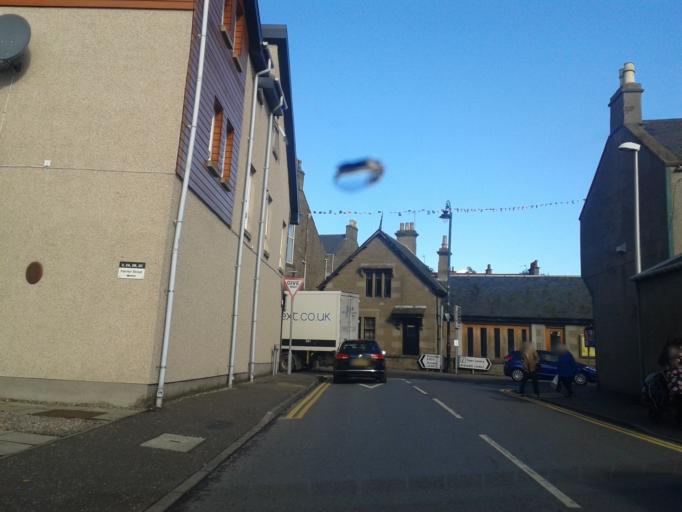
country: GB
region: Scotland
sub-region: Angus
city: Carnoustie
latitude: 56.5004
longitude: -2.7141
